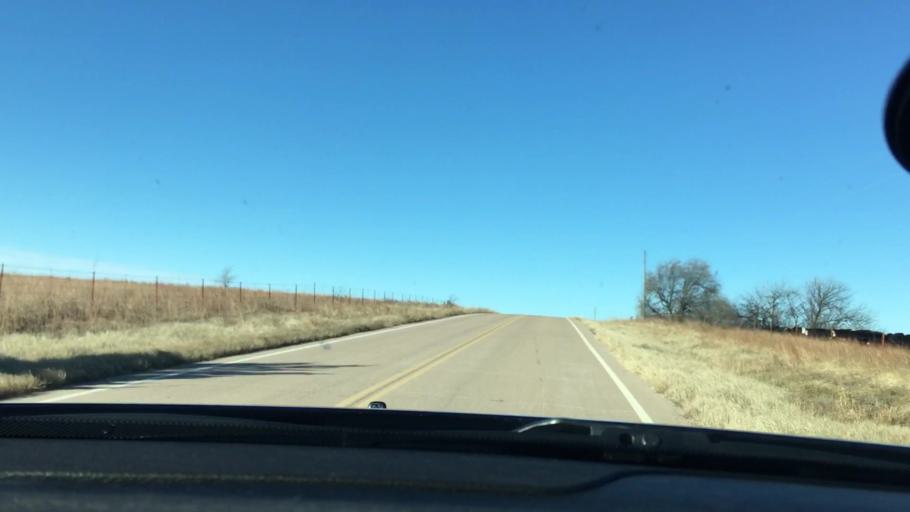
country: US
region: Oklahoma
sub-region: Marshall County
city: Madill
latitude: 34.1145
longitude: -96.7203
